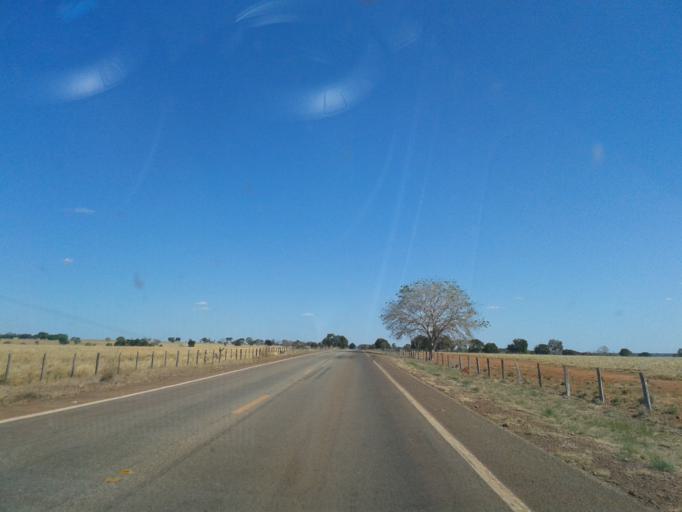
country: BR
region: Goias
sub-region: Crixas
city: Crixas
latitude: -14.1469
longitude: -50.3591
